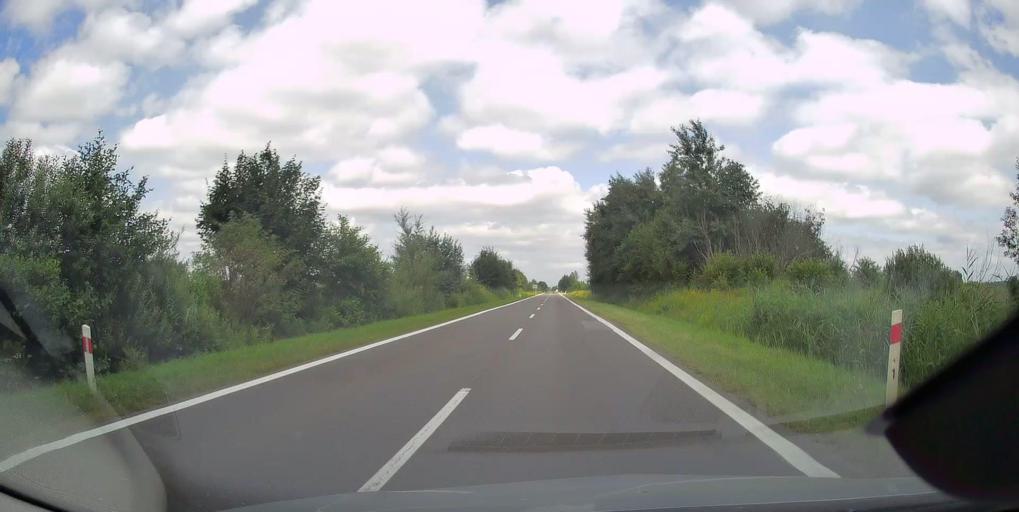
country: PL
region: Subcarpathian Voivodeship
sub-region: Powiat tarnobrzeski
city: Baranow Sandomierski
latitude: 50.4899
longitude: 21.5694
